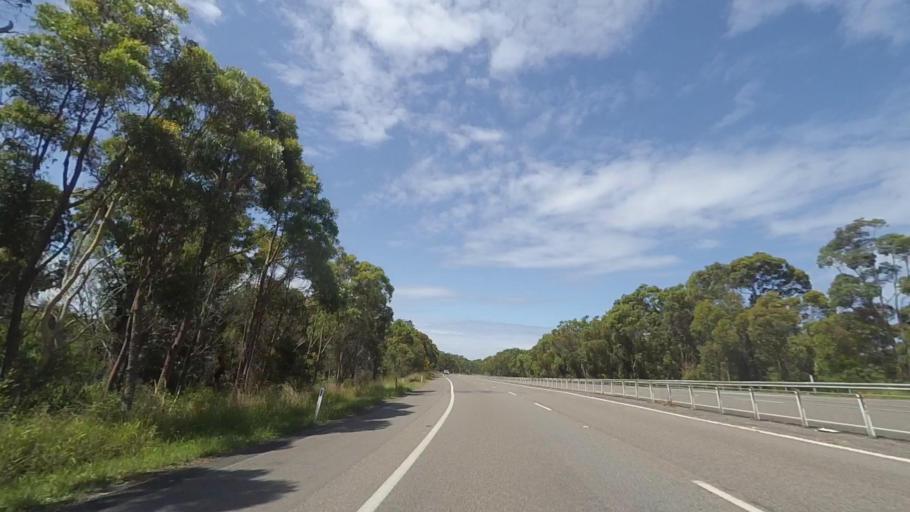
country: AU
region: New South Wales
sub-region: Wyong Shire
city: Kingfisher Shores
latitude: -33.1328
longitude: 151.6159
